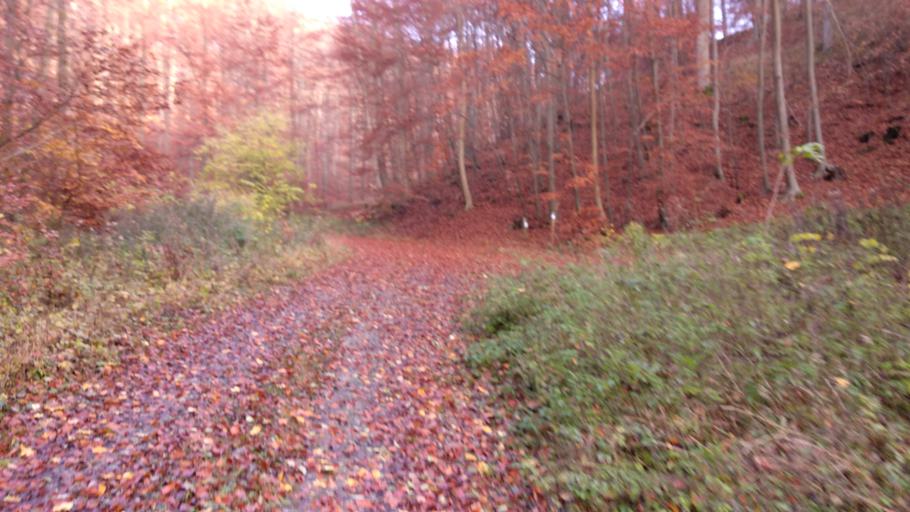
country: DE
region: North Rhine-Westphalia
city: Beverungen
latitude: 51.6574
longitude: 9.3314
